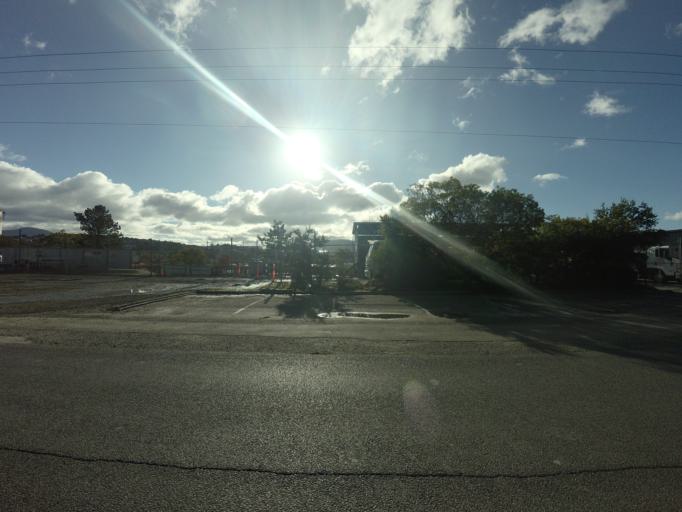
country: AU
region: Tasmania
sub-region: Glenorchy
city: Lutana
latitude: -42.8468
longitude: 147.3226
